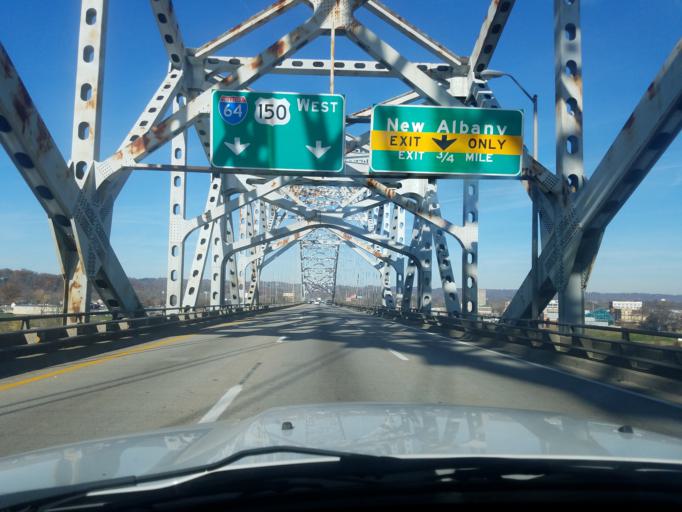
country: US
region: Indiana
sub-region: Floyd County
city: New Albany
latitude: 38.2782
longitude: -85.8217
